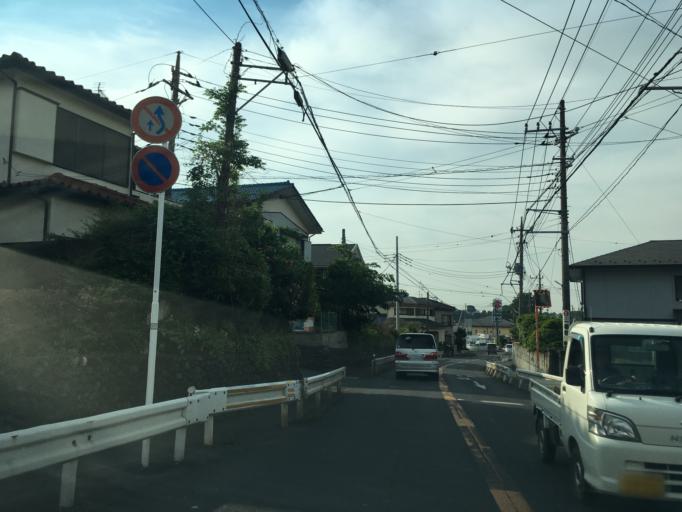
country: JP
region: Saitama
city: Tokorozawa
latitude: 35.7880
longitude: 139.5069
